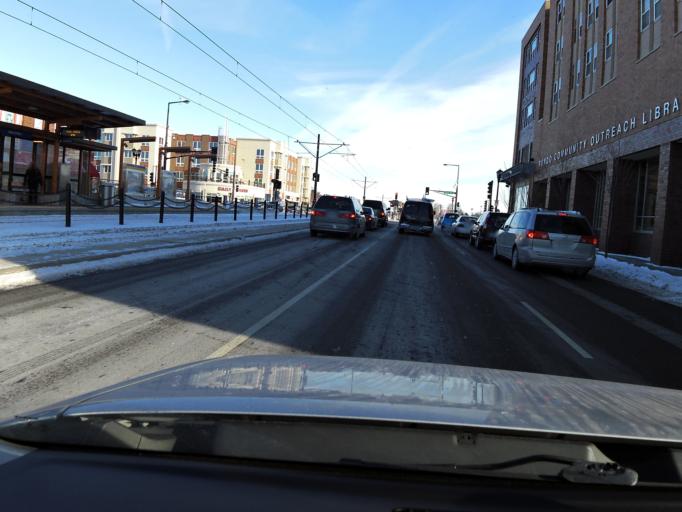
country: US
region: Minnesota
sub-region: Ramsey County
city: Saint Paul
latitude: 44.9556
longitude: -93.1271
